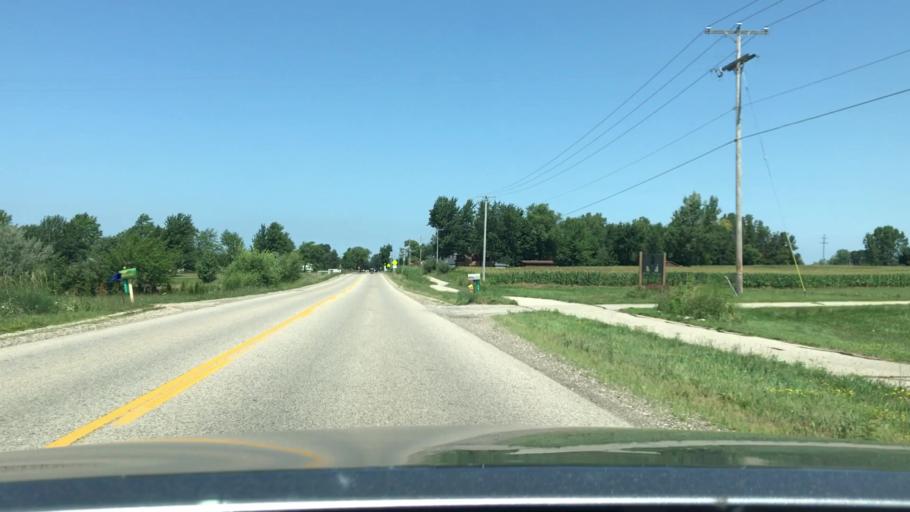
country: US
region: Michigan
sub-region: Ottawa County
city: Holland
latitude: 42.8495
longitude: -86.0791
